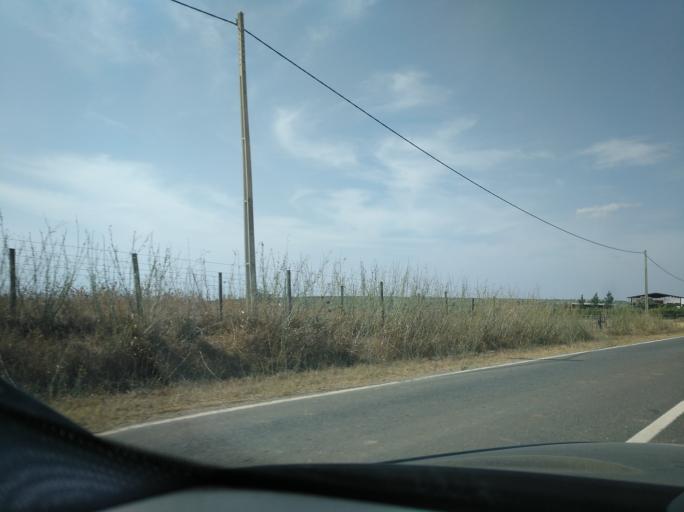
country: PT
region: Beja
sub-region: Beja
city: Beja
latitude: 37.8603
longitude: -7.8623
